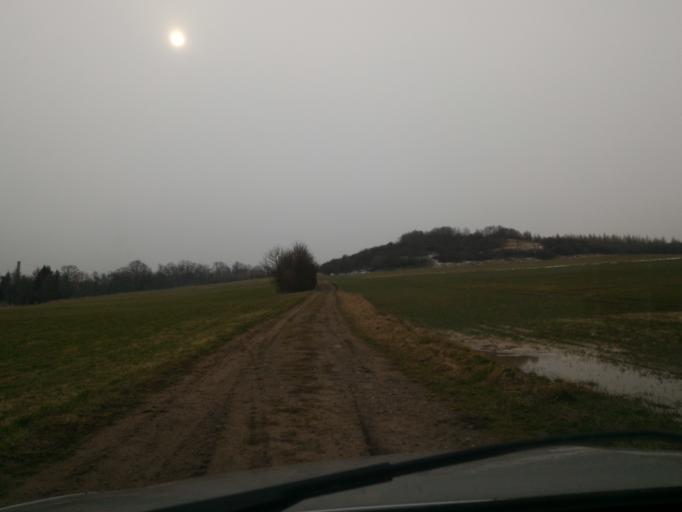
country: DE
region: Saxony
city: Grossschonau
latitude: 50.8982
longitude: 14.6501
